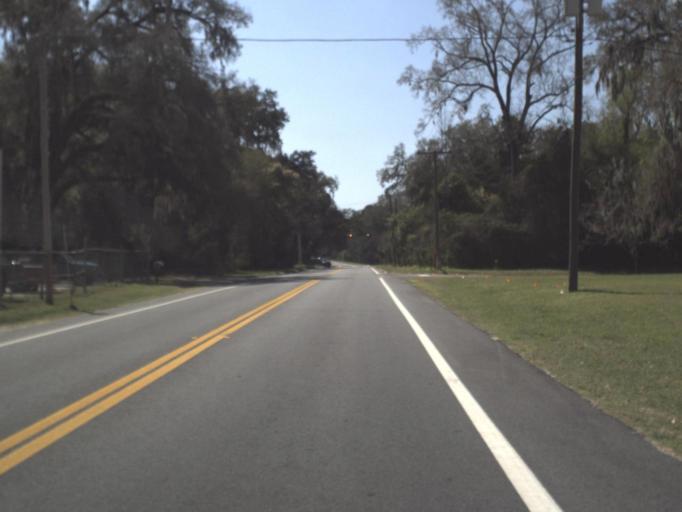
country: US
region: Florida
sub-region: Jefferson County
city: Monticello
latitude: 30.4797
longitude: -84.0227
